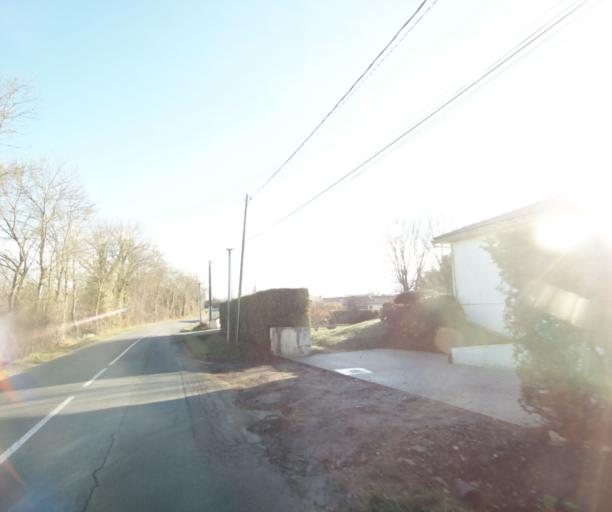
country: FR
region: Poitou-Charentes
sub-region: Departement de la Charente-Maritime
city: Fontcouverte
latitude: 45.7483
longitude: -0.5839
